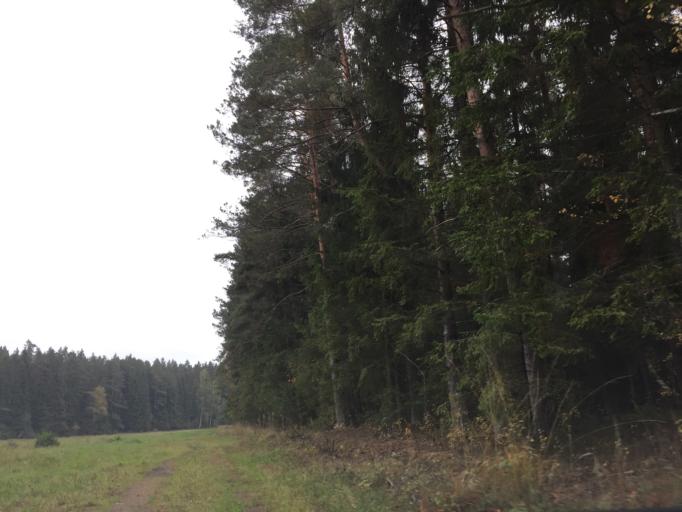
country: LV
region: Jelgava
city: Jelgava
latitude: 56.7322
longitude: 23.6900
